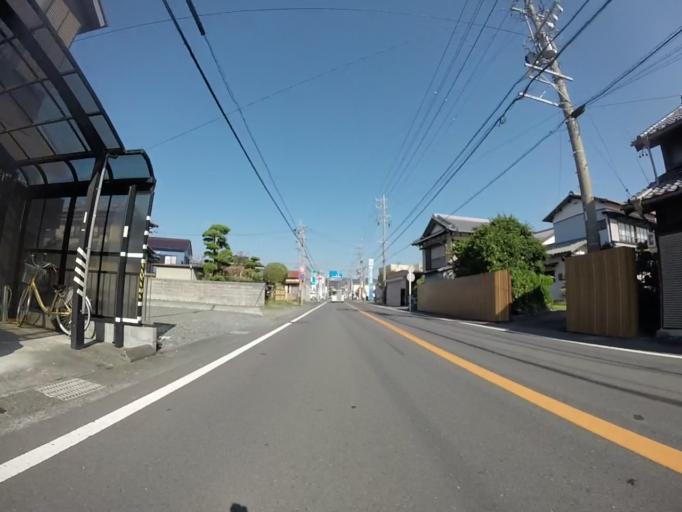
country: JP
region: Shizuoka
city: Fujieda
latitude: 34.8816
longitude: 138.2638
